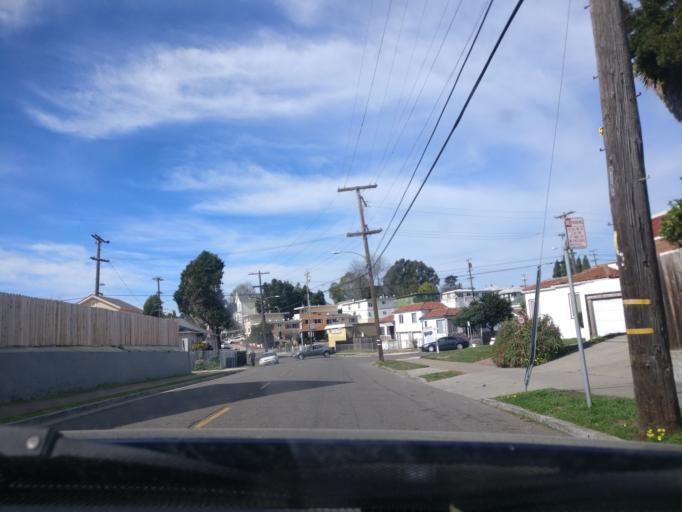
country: US
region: California
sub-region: Alameda County
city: Piedmont
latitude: 37.7931
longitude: -122.2255
